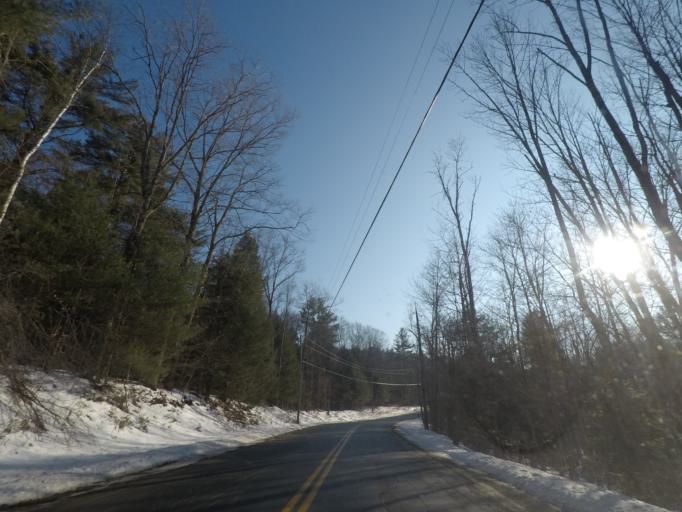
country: US
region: Massachusetts
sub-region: Berkshire County
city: Richmond
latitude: 42.5190
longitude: -73.4160
